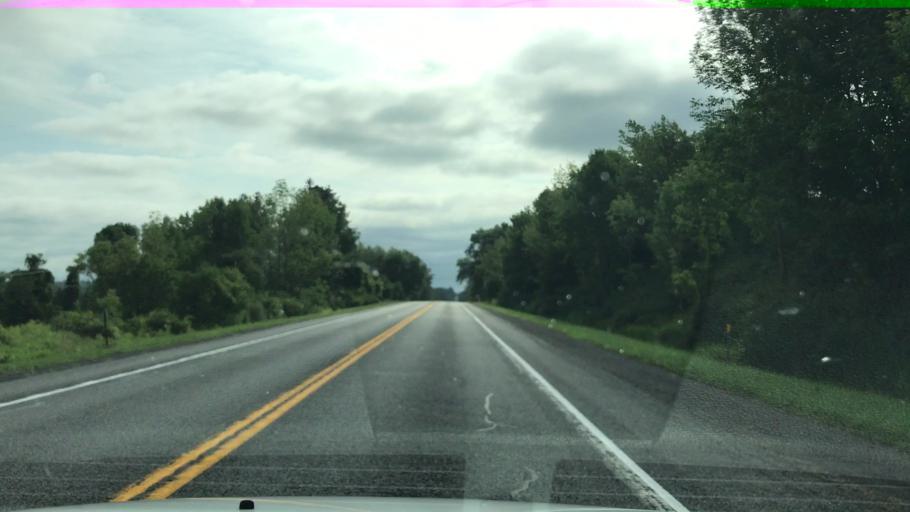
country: US
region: New York
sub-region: Erie County
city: Alden
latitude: 42.8351
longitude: -78.4383
